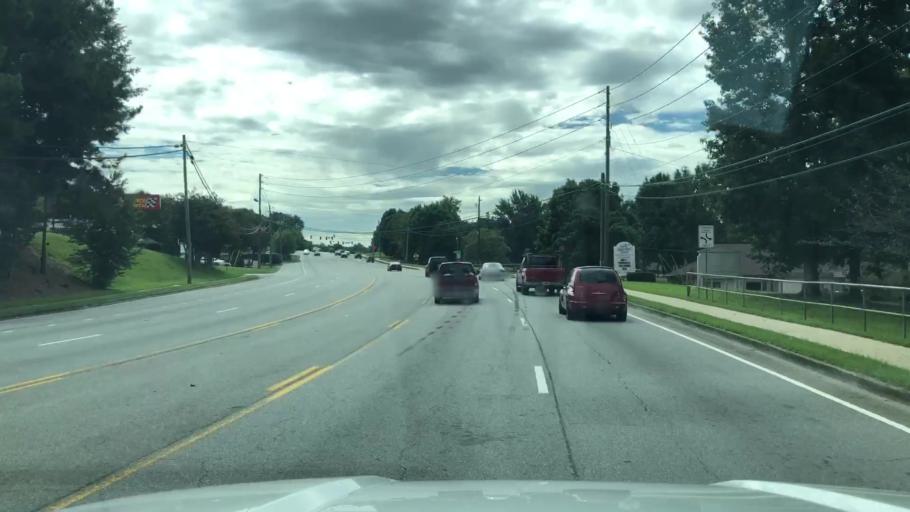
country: US
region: Georgia
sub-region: Gwinnett County
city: Norcross
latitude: 33.9614
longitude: -84.2495
